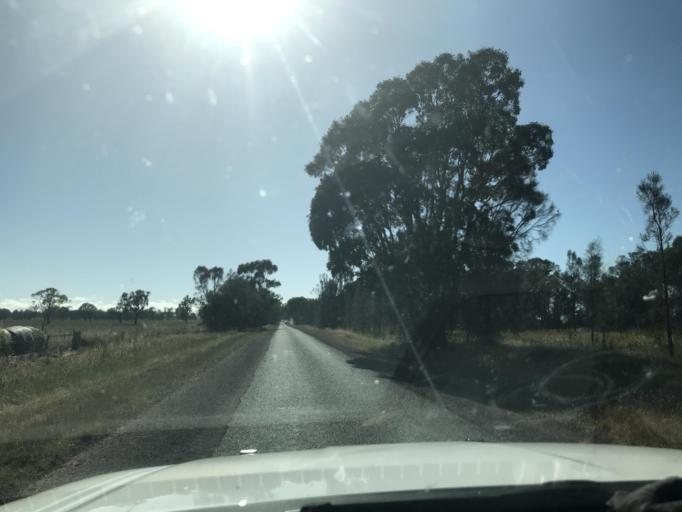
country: AU
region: Victoria
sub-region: Horsham
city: Horsham
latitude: -37.0068
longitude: 141.6383
